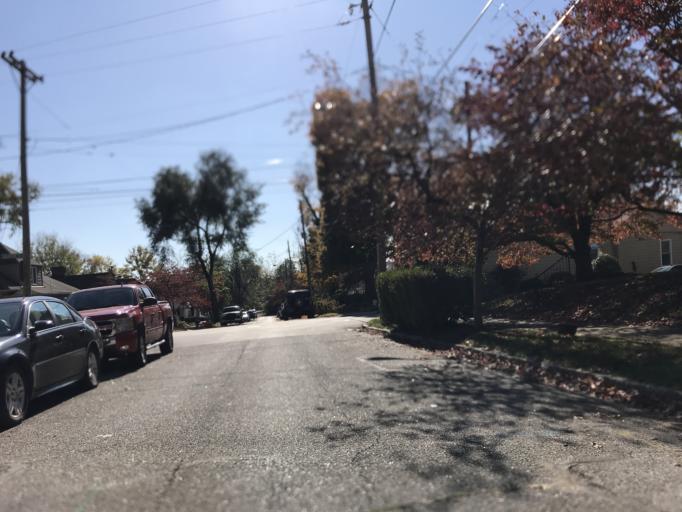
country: US
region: Indiana
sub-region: Clark County
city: Jeffersonville
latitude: 38.2551
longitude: -85.7148
